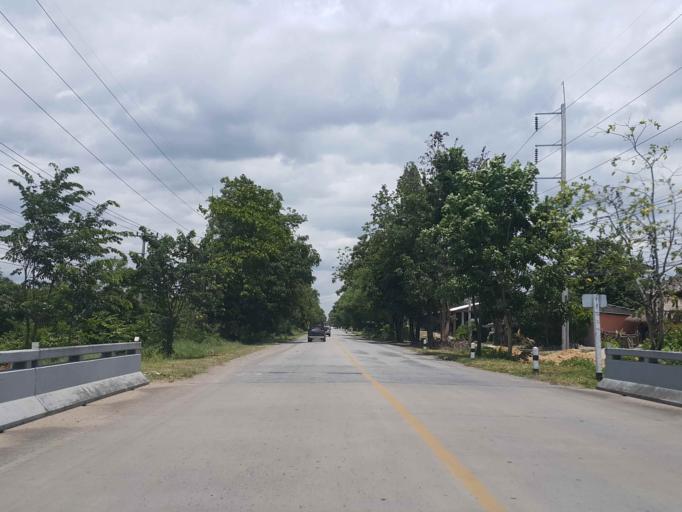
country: TH
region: Lamphun
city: Ban Hong
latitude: 18.3859
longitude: 98.8209
